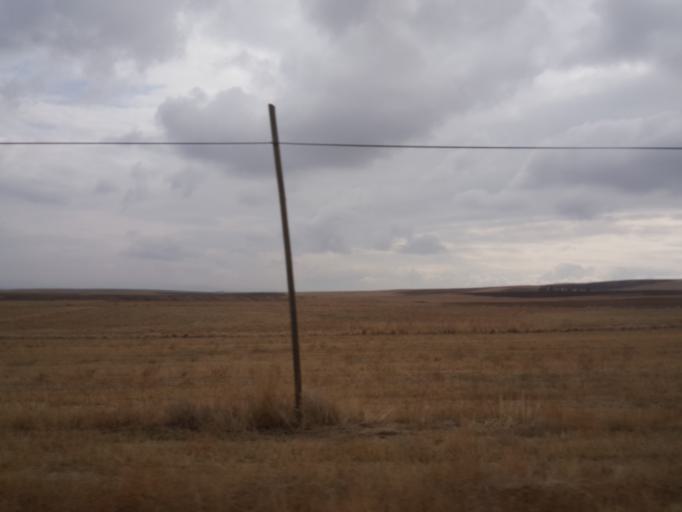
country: TR
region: Kirikkale
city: Celebi
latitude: 39.5564
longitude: 33.5734
